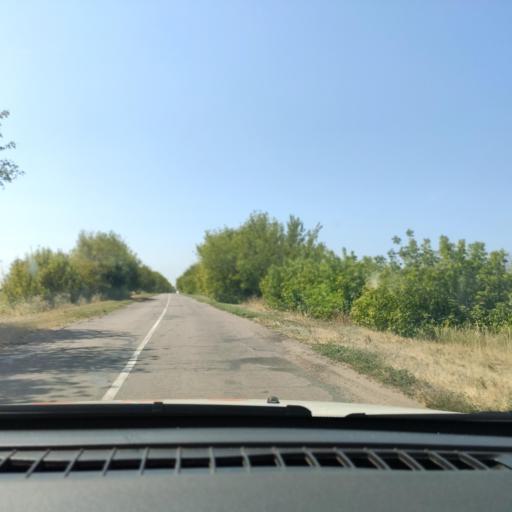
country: RU
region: Voronezj
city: Imeni Pervogo Maya
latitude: 50.7165
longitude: 39.3473
